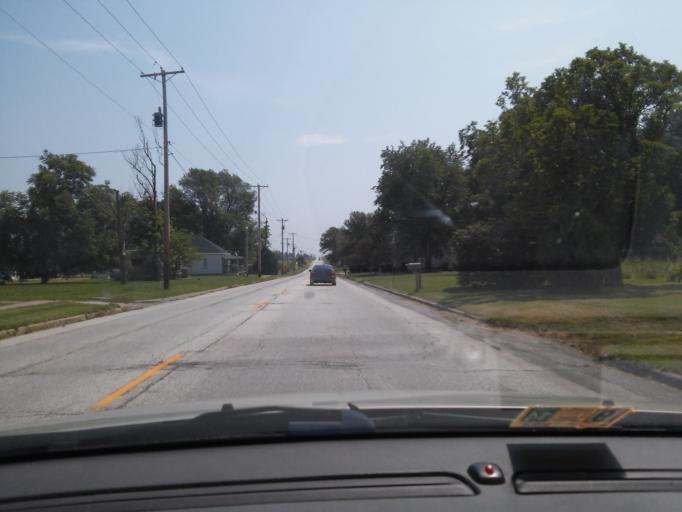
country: US
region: Missouri
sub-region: Pike County
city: Bowling Green
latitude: 39.3454
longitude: -91.3396
